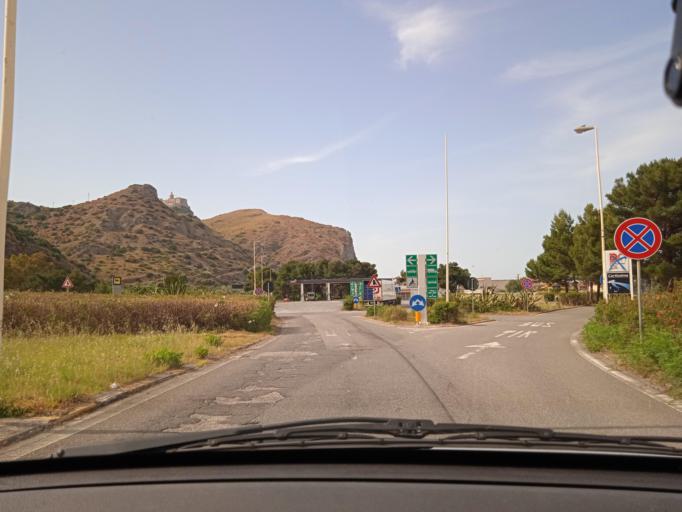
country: IT
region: Sicily
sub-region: Messina
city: Oliveri
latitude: 38.1267
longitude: 15.0539
